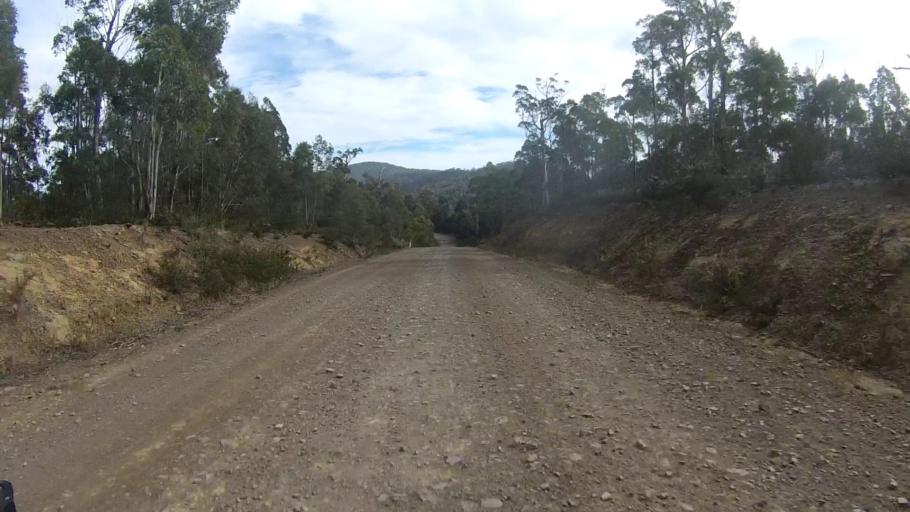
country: AU
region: Tasmania
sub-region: Sorell
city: Sorell
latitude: -42.7583
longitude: 147.8294
